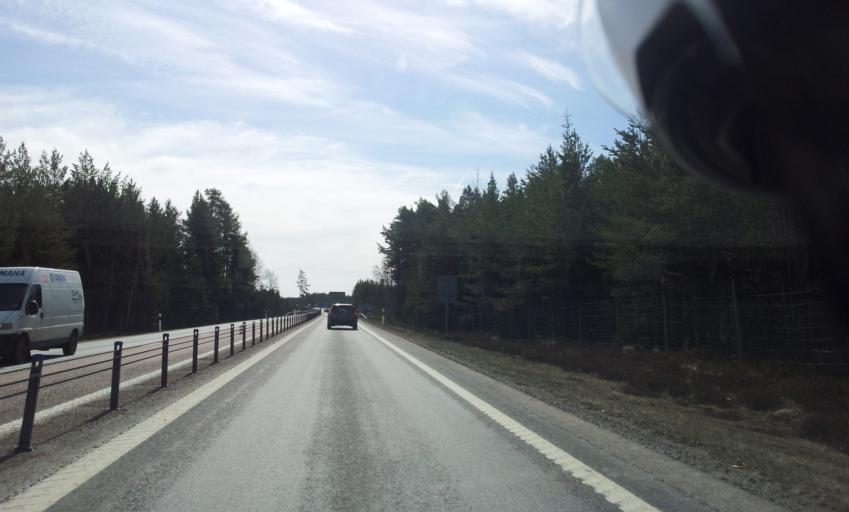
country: SE
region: Gaevleborg
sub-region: Gavle Kommun
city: Norrsundet
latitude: 61.0476
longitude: 16.9600
